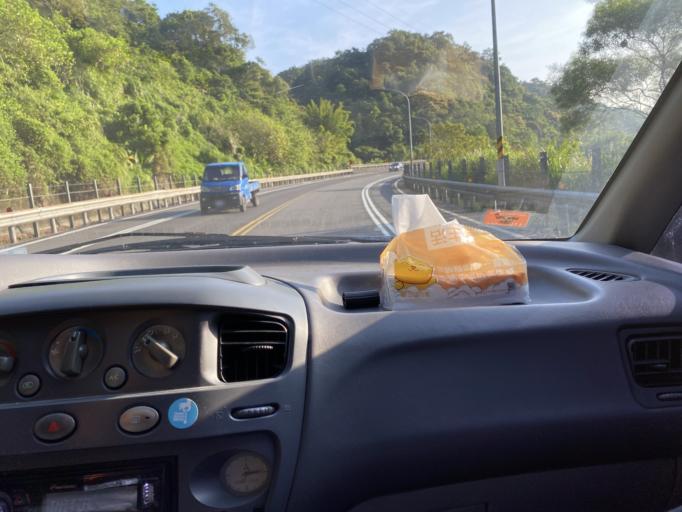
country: TW
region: Taiwan
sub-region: Keelung
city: Keelung
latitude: 25.0224
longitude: 121.8152
